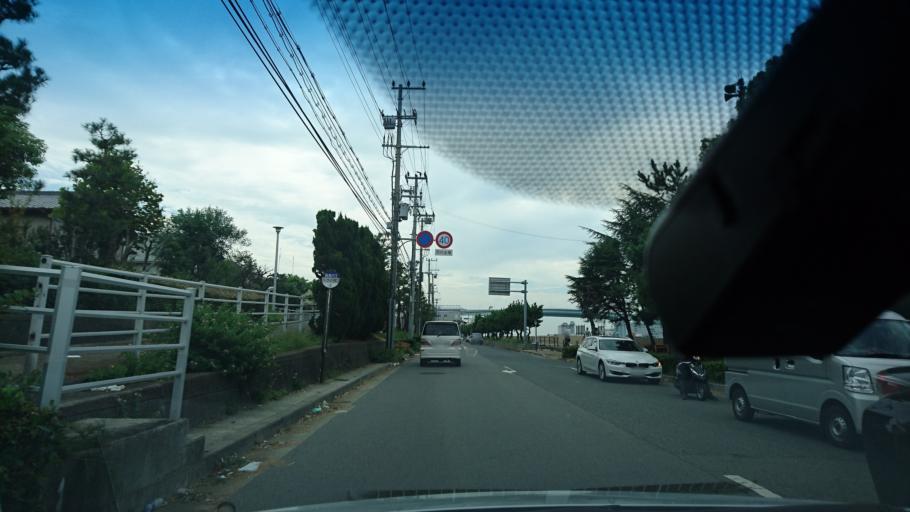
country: JP
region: Hyogo
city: Ashiya
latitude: 34.7192
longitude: 135.3057
